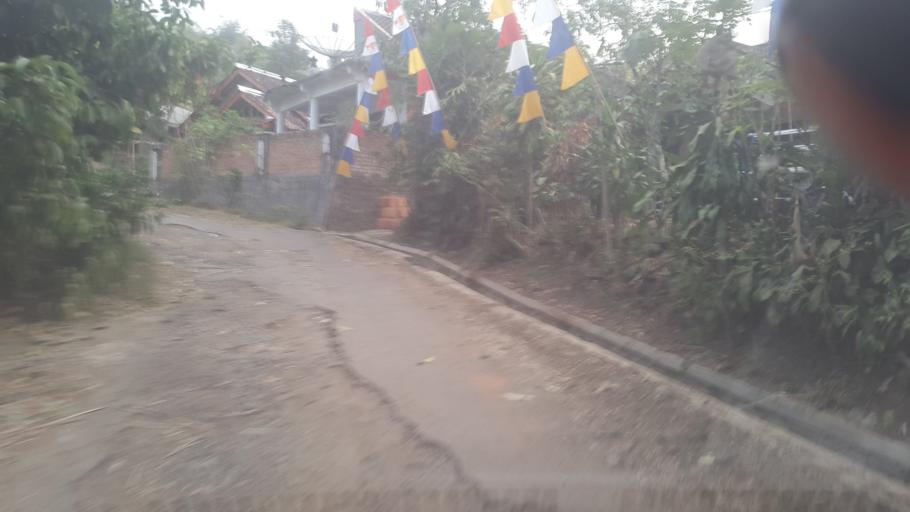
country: ID
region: West Java
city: Sukamaju
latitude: -7.0058
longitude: 106.8925
